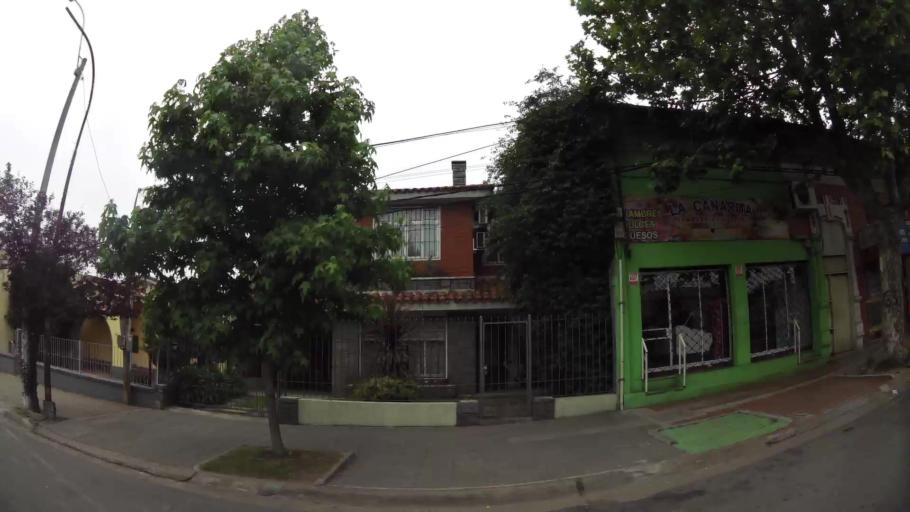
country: UY
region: Canelones
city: Las Piedras
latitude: -34.7281
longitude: -56.2212
